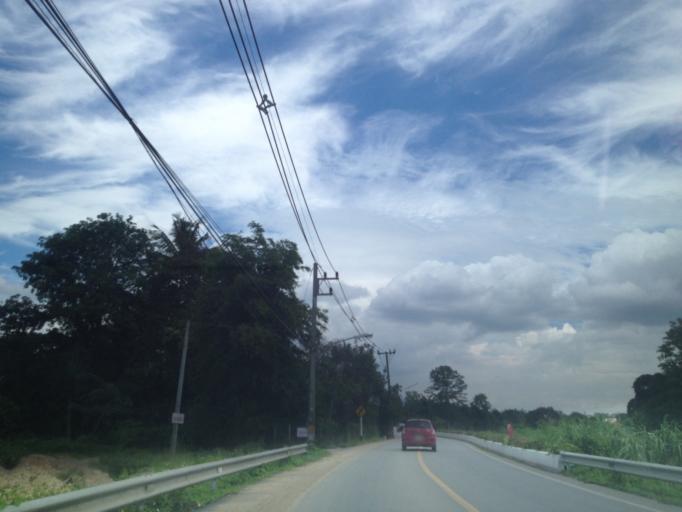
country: TH
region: Chiang Mai
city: Saraphi
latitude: 18.7276
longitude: 98.9854
